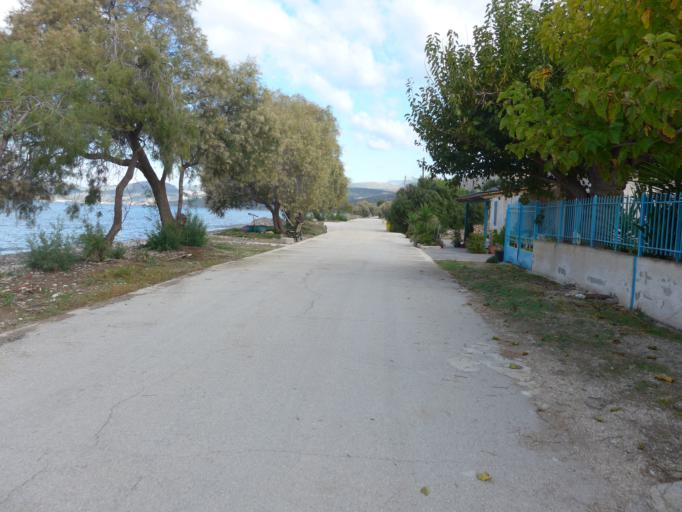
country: GR
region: Peloponnese
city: Asklipieio
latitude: 37.4882
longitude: 22.9920
